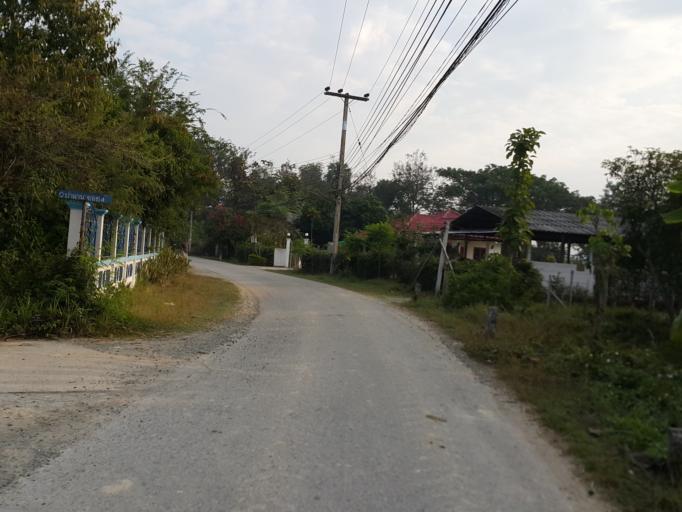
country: TH
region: Chiang Mai
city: San Sai
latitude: 18.8186
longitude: 99.1019
